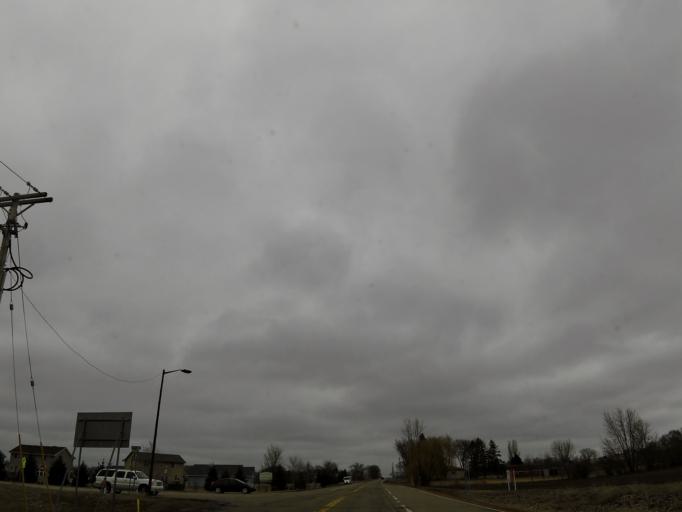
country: US
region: Minnesota
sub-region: Scott County
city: Shakopee
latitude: 44.7717
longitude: -93.5410
